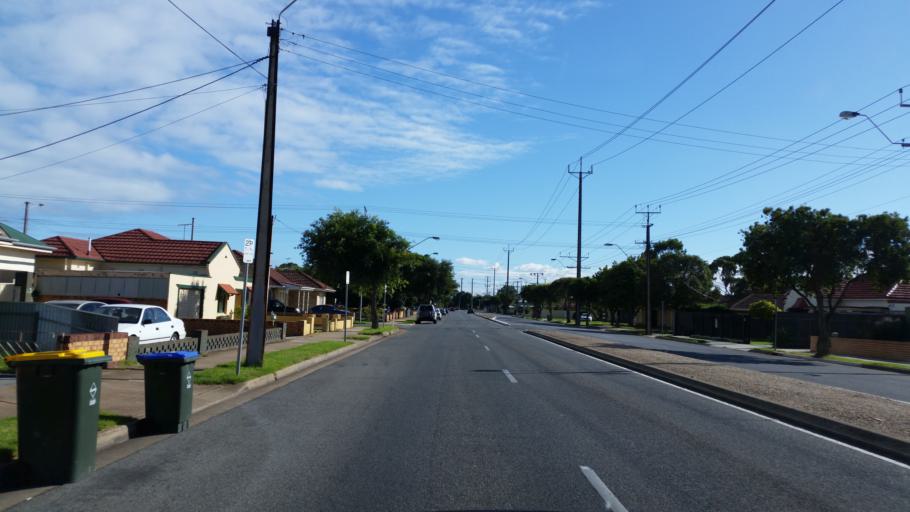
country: AU
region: South Australia
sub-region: Charles Sturt
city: Woodville West
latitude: -34.8821
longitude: 138.5309
